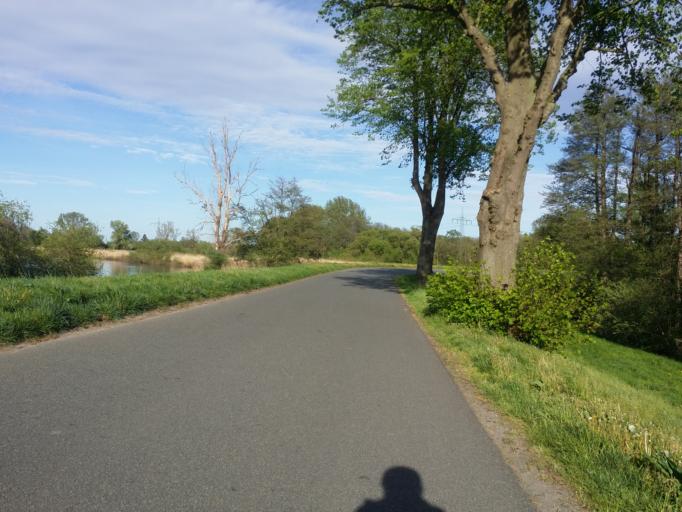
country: DE
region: Lower Saxony
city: Ritterhude
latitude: 53.1633
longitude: 8.7431
